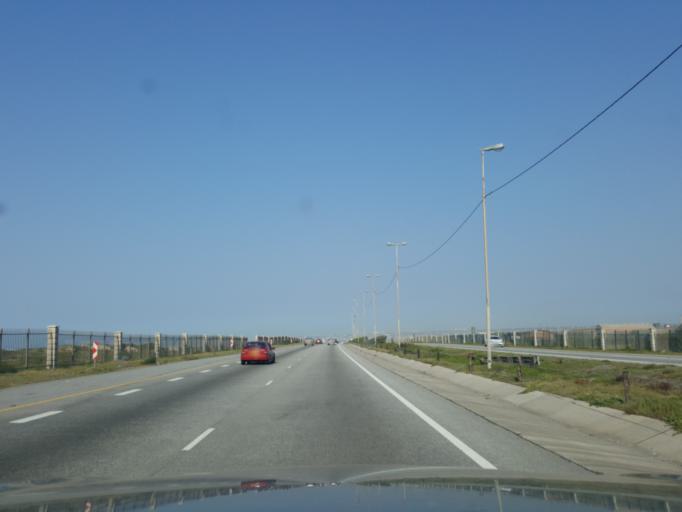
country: ZA
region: Eastern Cape
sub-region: Nelson Mandela Bay Metropolitan Municipality
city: Port Elizabeth
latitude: -33.8867
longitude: 25.6230
